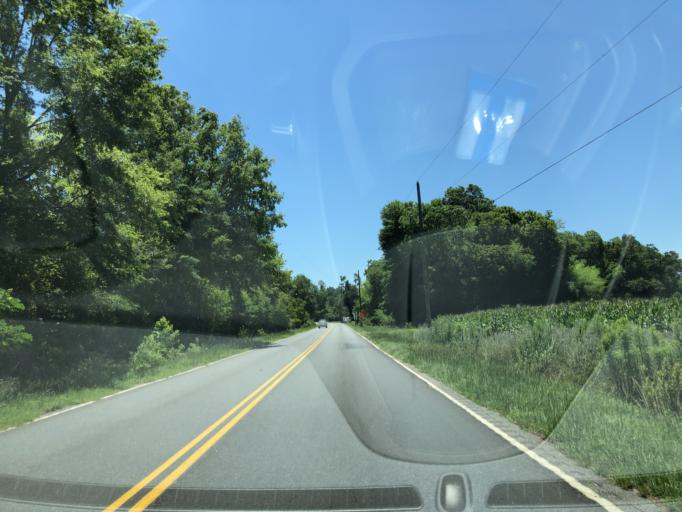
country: US
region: South Carolina
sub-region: Barnwell County
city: Blackville
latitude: 33.3550
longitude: -81.2788
